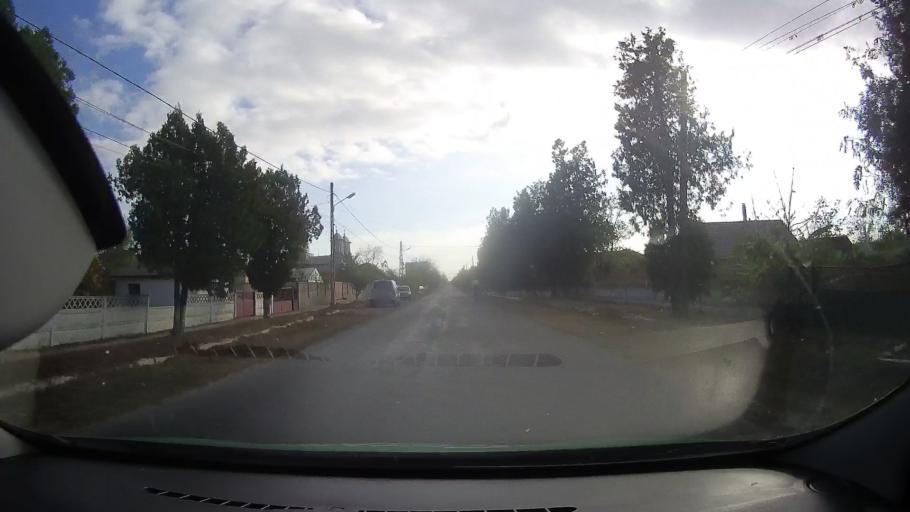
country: RO
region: Constanta
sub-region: Comuna Corbu
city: Corbu
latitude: 44.4158
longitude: 28.6610
